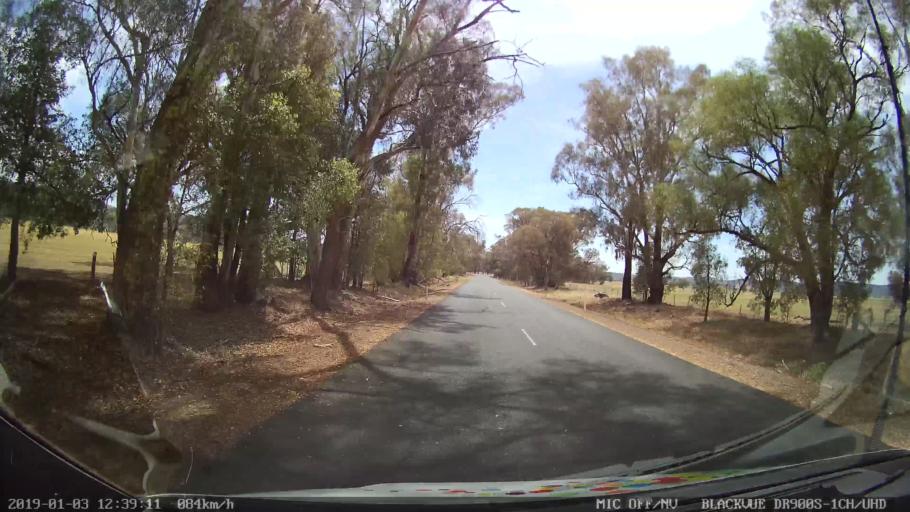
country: AU
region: New South Wales
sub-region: Weddin
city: Grenfell
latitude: -33.8270
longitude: 148.2037
